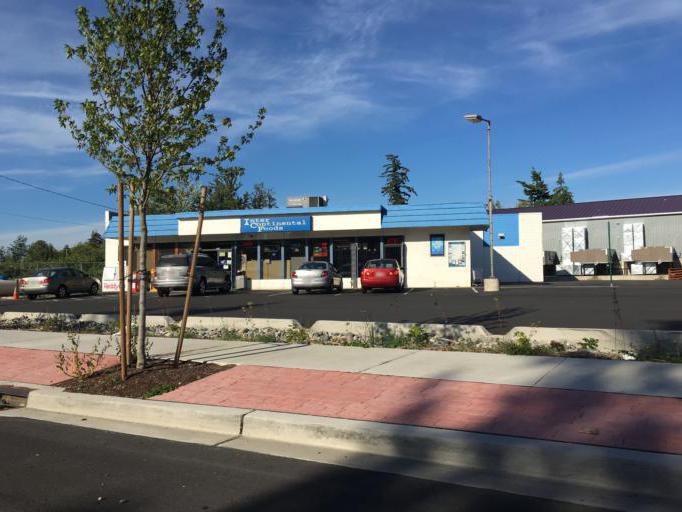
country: US
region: Washington
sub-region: Whatcom County
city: Bellingham
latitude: 48.8062
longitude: -122.4859
